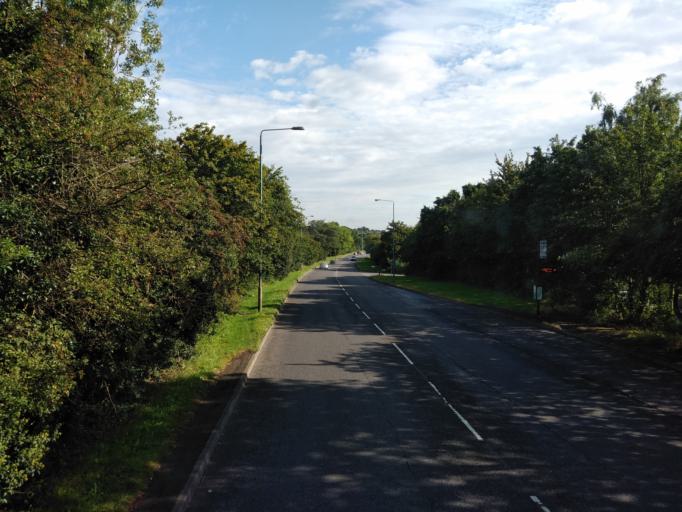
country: GB
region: England
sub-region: Nottinghamshire
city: Kimberley
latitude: 52.9568
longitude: -1.2453
